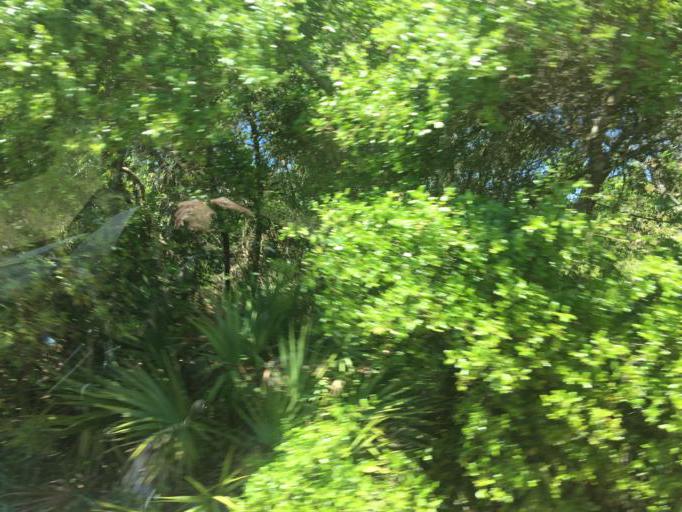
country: US
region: Florida
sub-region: Bay County
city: Laguna Beach
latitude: 30.2561
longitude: -85.9392
